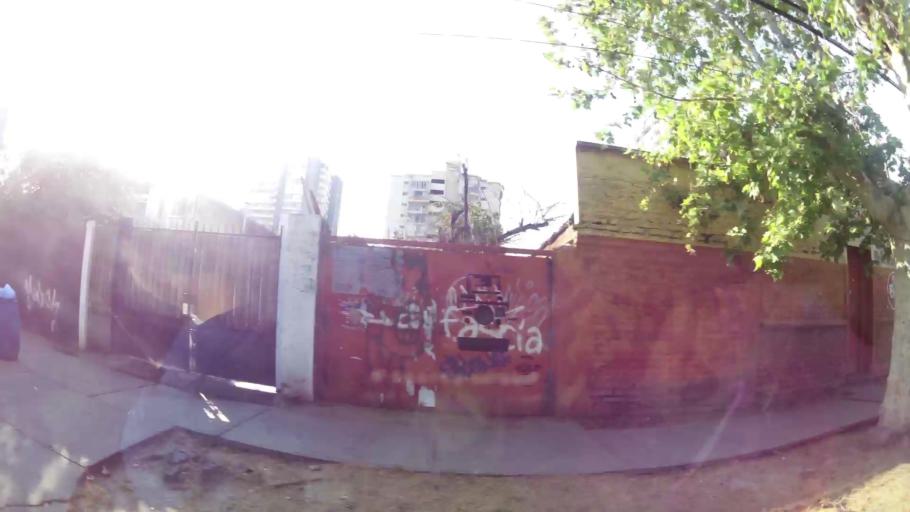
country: CL
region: Santiago Metropolitan
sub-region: Provincia de Santiago
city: Santiago
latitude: -33.5114
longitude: -70.6603
